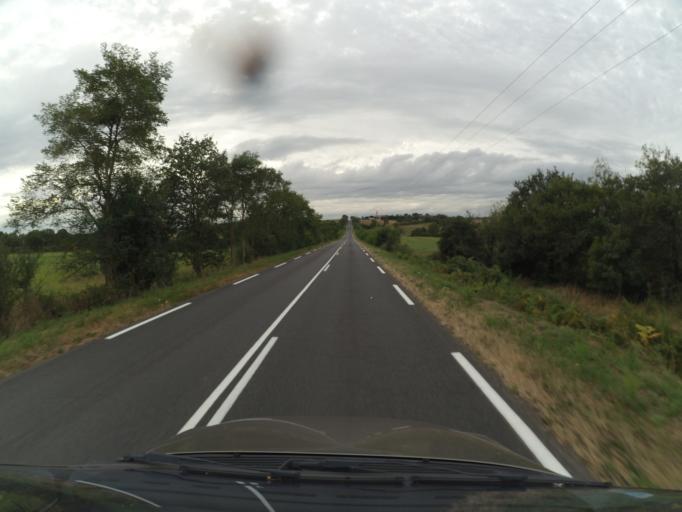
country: FR
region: Pays de la Loire
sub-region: Departement de Maine-et-Loire
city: Le Longeron
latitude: 47.0260
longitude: -1.0665
